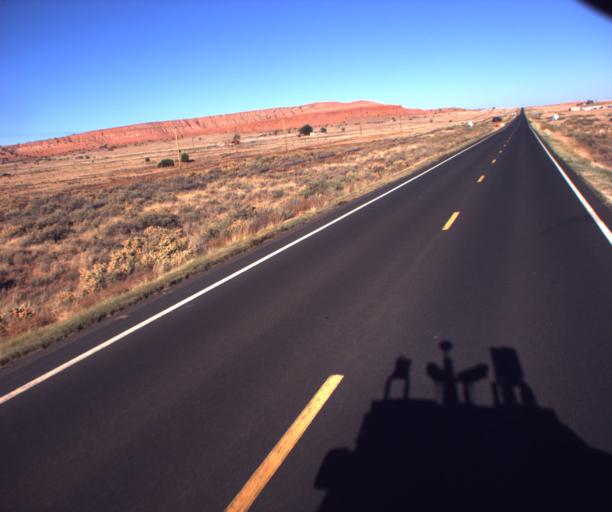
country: US
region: Arizona
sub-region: Apache County
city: Ganado
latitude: 35.7606
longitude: -109.6344
